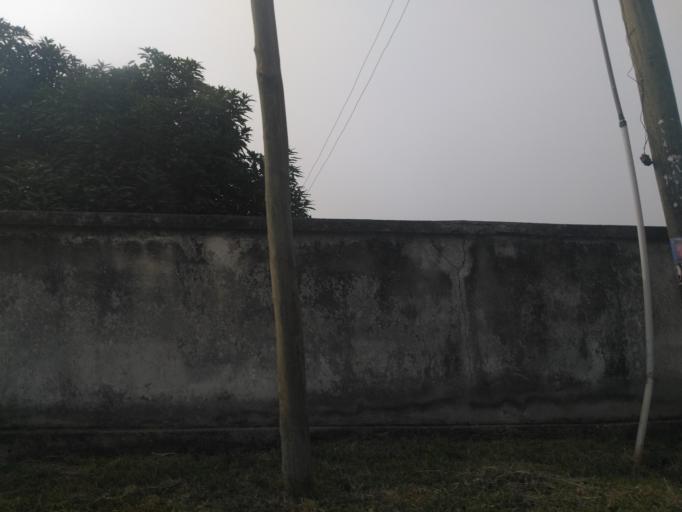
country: GH
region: Ashanti
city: Kumasi
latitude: 6.6662
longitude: -1.6156
